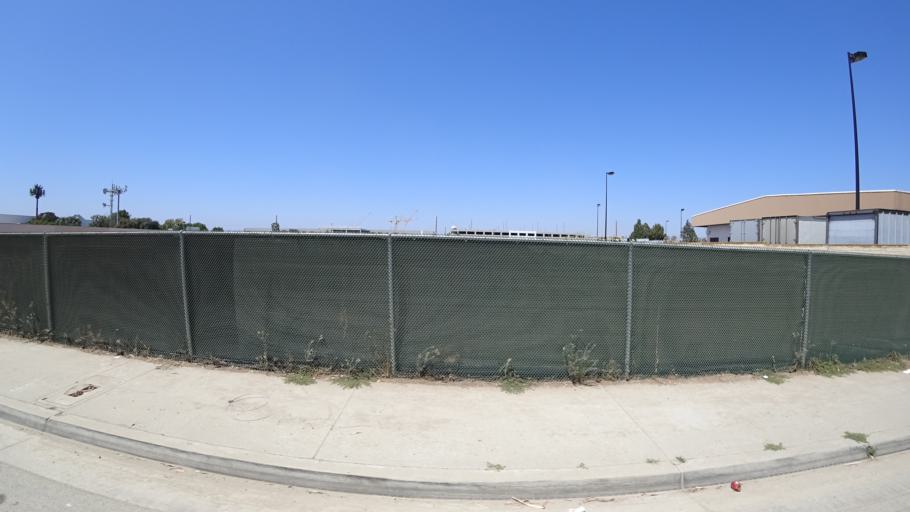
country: US
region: California
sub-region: Los Angeles County
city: Lennox
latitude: 33.9437
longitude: -118.3374
